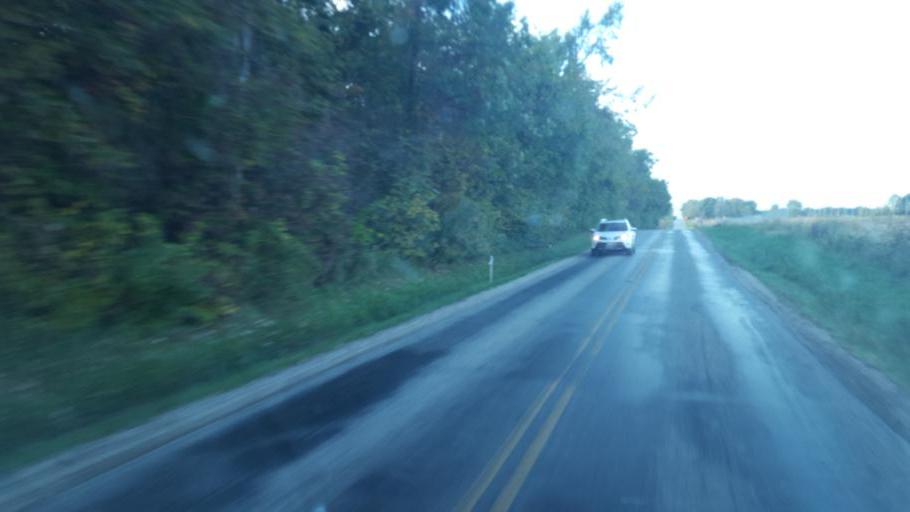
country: US
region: Ohio
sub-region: Franklin County
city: New Albany
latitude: 40.0580
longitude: -82.7551
